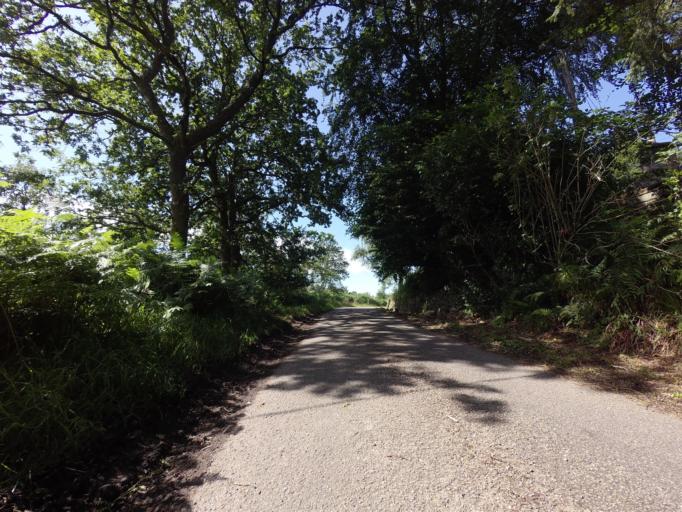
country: GB
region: Scotland
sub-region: Highland
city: Nairn
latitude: 57.5041
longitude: -3.9119
